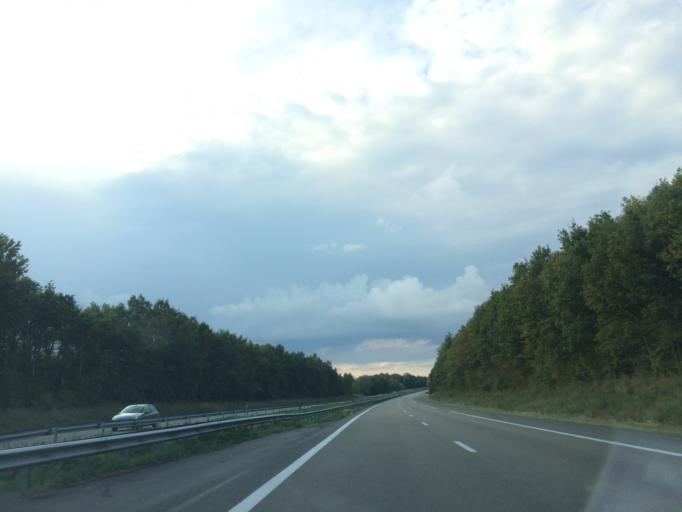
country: FR
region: Ile-de-France
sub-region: Departement de Seine-et-Marne
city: Egreville
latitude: 48.1377
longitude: 2.9192
